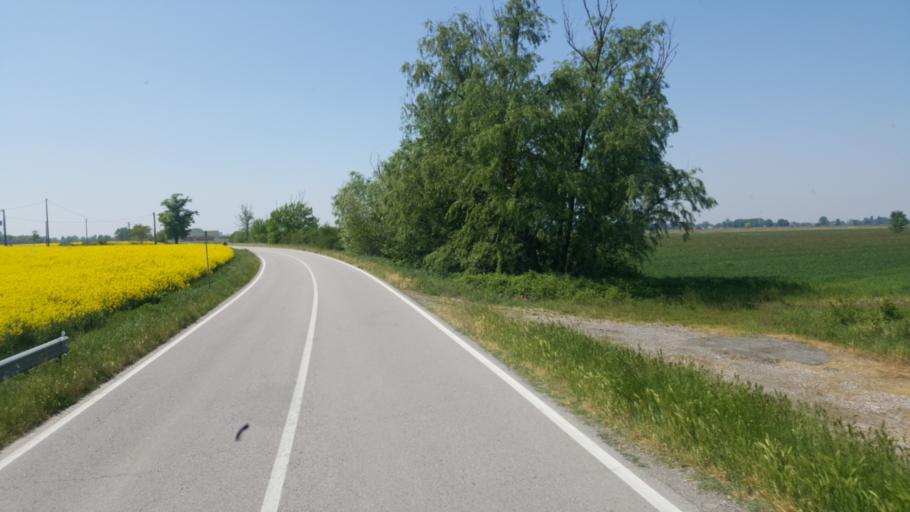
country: IT
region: Lombardy
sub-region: Provincia di Mantova
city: Pieve di Coriano
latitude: 45.0271
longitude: 11.0841
